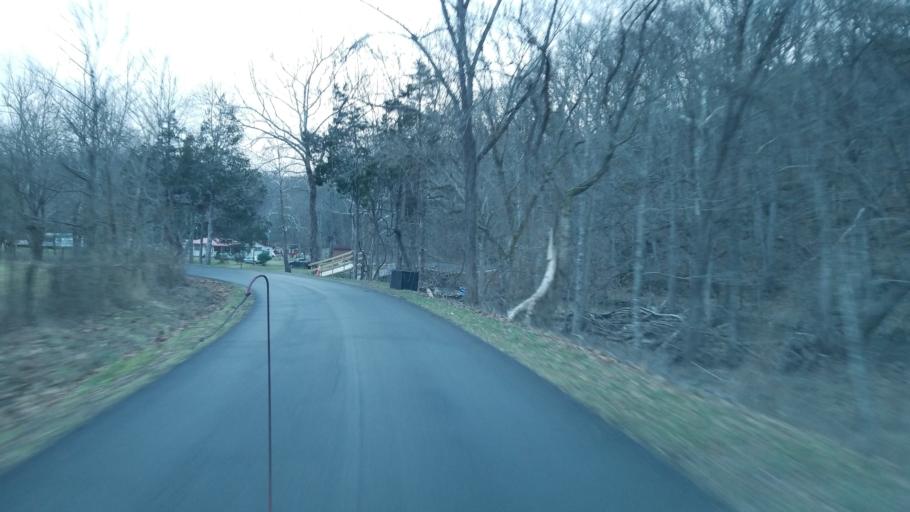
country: US
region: Virginia
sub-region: Pulaski County
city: Pulaski
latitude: 37.1564
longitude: -80.8690
